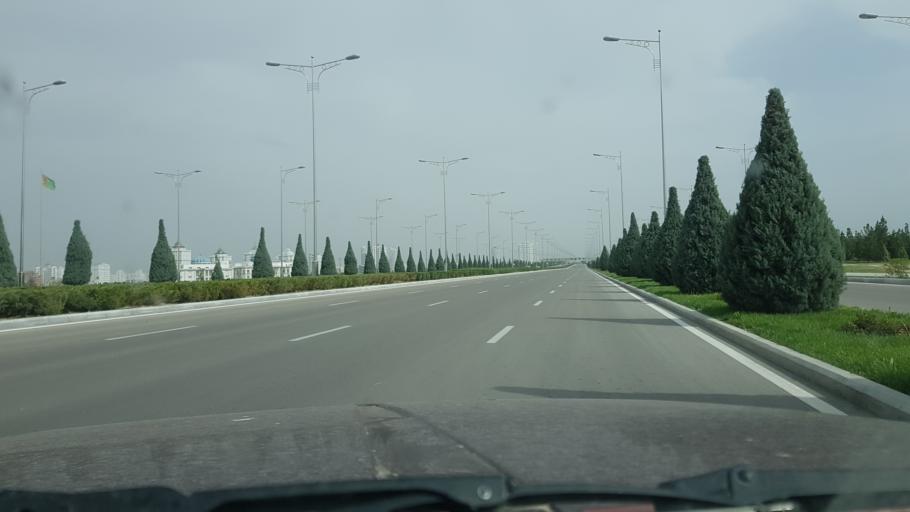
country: TM
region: Ahal
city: Ashgabat
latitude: 37.8860
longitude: 58.3405
